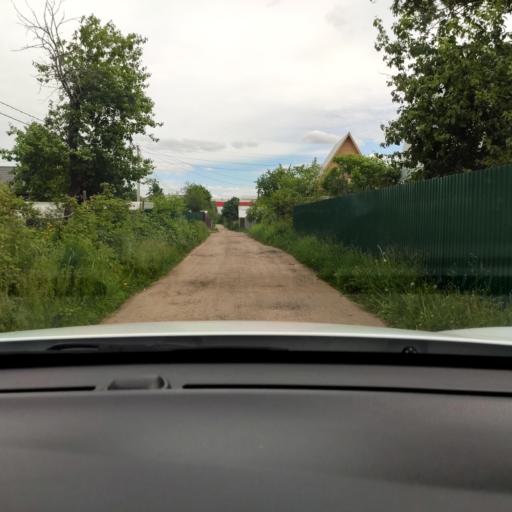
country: RU
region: Tatarstan
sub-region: Gorod Kazan'
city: Kazan
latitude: 55.8705
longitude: 49.1067
